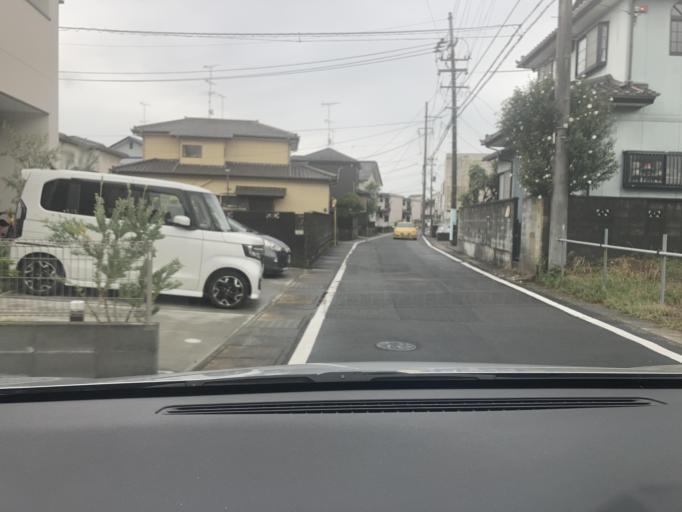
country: JP
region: Fukushima
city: Iwaki
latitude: 36.9636
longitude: 140.9029
